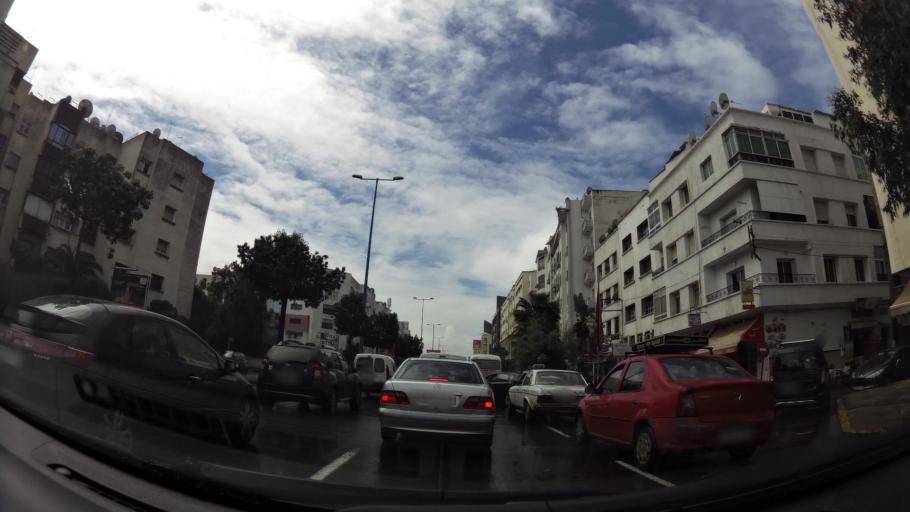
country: MA
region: Grand Casablanca
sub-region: Casablanca
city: Casablanca
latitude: 33.5716
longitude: -7.6424
